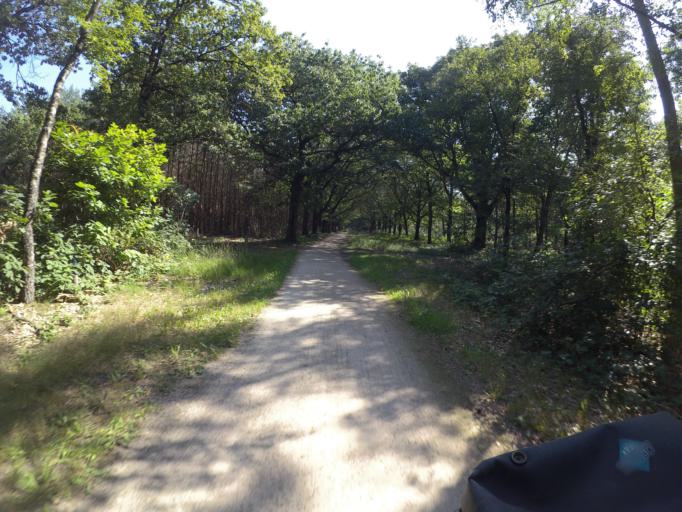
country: NL
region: North Brabant
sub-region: Gemeente Mill en Sint Hubert
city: Wilbertoord
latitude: 51.6187
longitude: 5.8147
